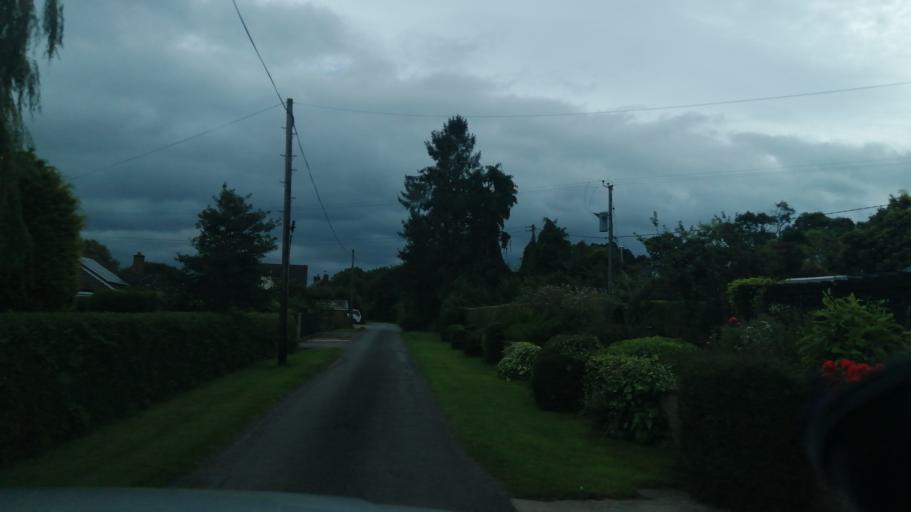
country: GB
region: England
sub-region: Herefordshire
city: Thruxton
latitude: 52.0151
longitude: -2.7956
